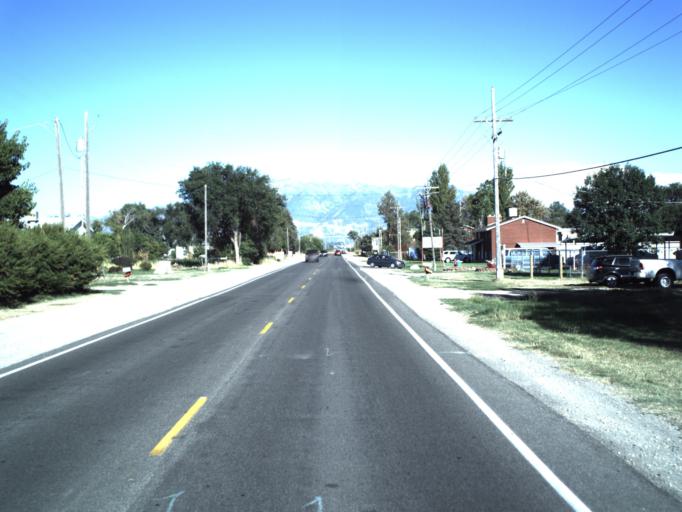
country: US
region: Utah
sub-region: Weber County
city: Hooper
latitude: 41.1907
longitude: -112.1069
